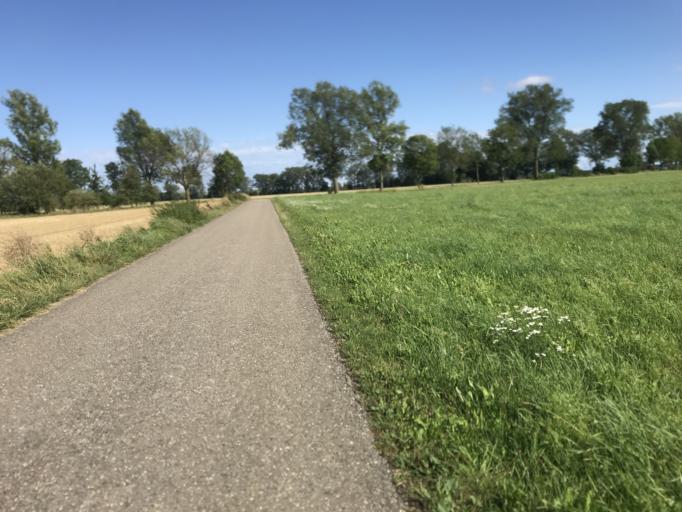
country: DE
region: Baden-Wuerttemberg
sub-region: Tuebingen Region
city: Langenau
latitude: 48.4746
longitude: 10.1223
